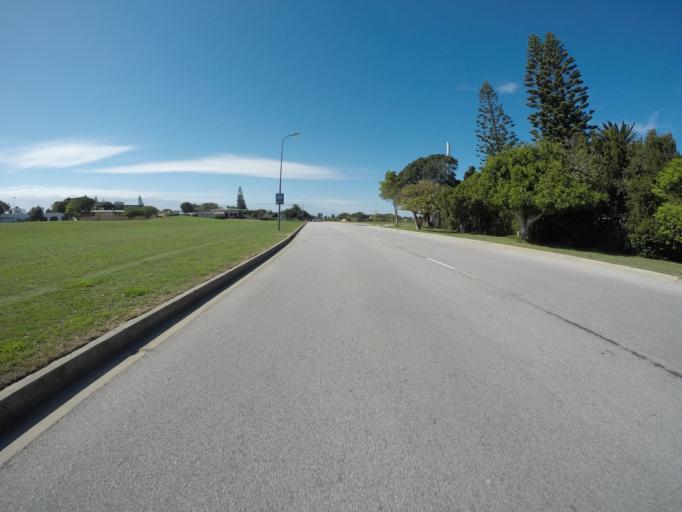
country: ZA
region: Eastern Cape
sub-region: Nelson Mandela Bay Metropolitan Municipality
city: Port Elizabeth
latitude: -33.9918
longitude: 25.6546
